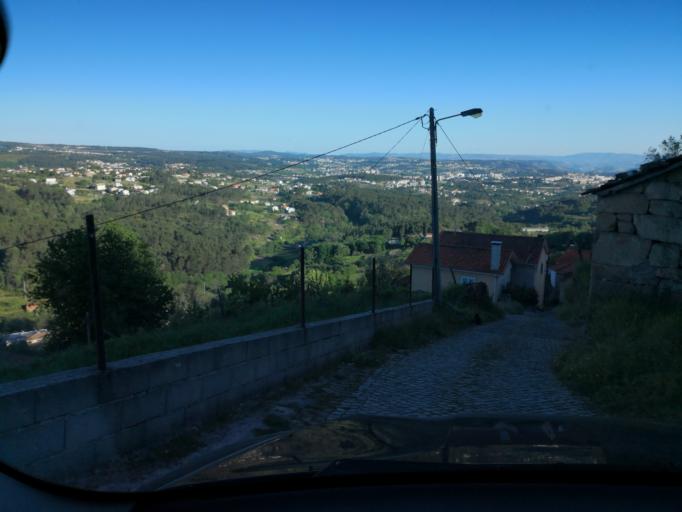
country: PT
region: Vila Real
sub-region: Vila Real
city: Vila Real
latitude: 41.3453
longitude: -7.7375
